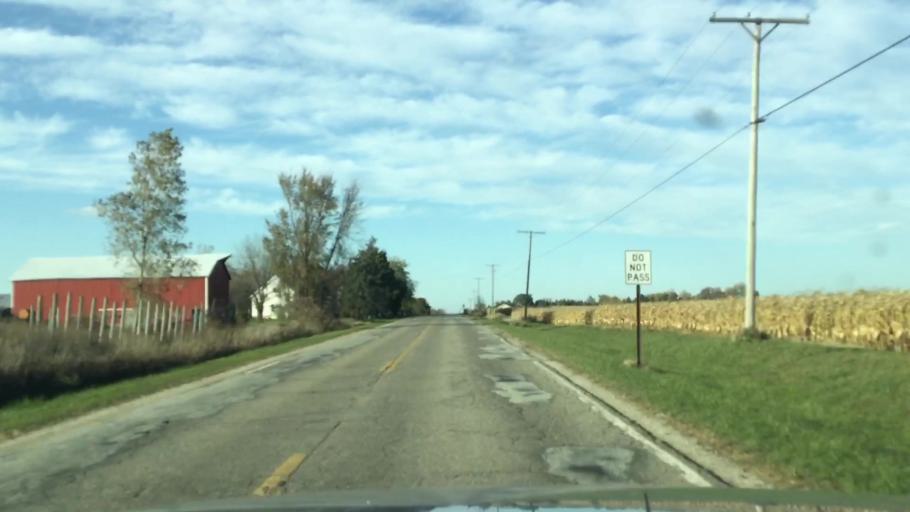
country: US
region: Michigan
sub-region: Lapeer County
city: North Branch
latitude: 43.2755
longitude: -83.1982
